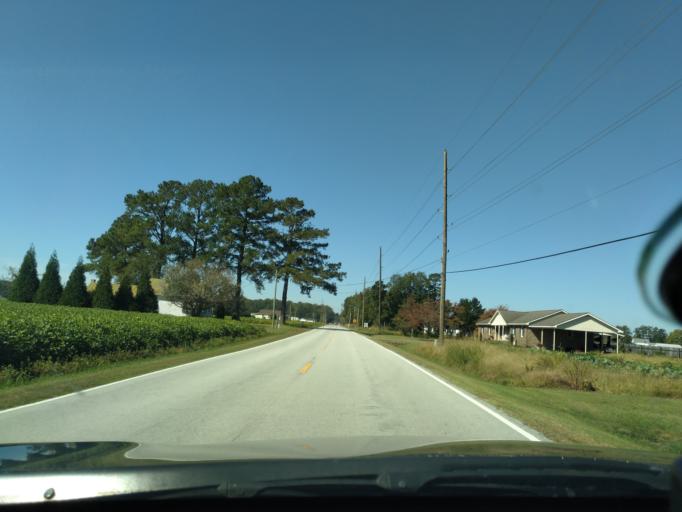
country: US
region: North Carolina
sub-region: Beaufort County
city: River Road
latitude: 35.5759
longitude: -76.9377
